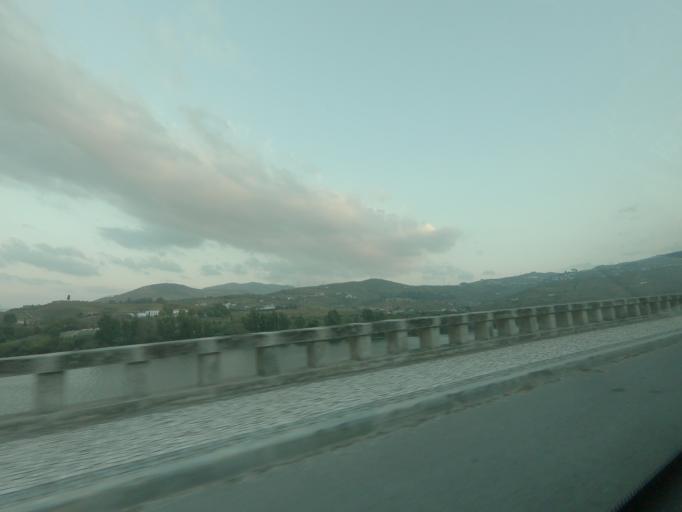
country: PT
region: Vila Real
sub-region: Peso da Regua
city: Godim
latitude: 41.1591
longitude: -7.8062
